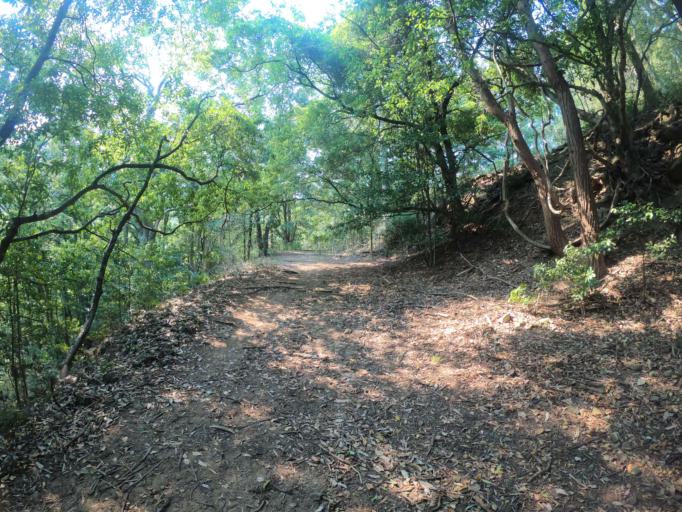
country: AU
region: New South Wales
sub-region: Wollongong
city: Bulli
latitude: -34.3251
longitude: 150.8883
